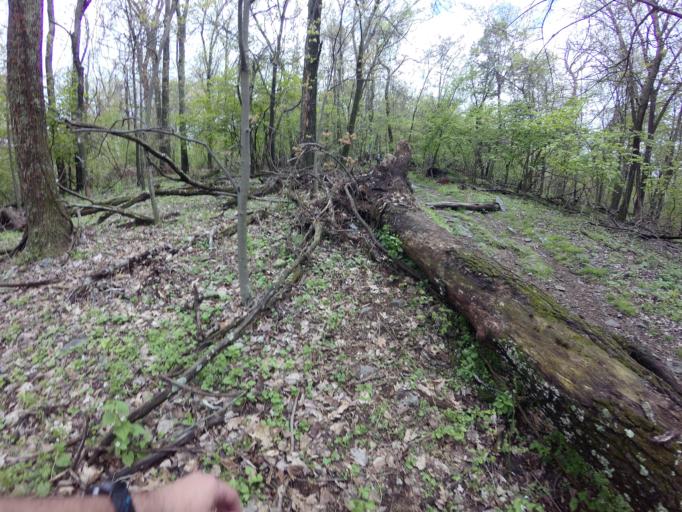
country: US
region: Maryland
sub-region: Washington County
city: Boonsboro
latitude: 39.5094
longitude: -77.6211
